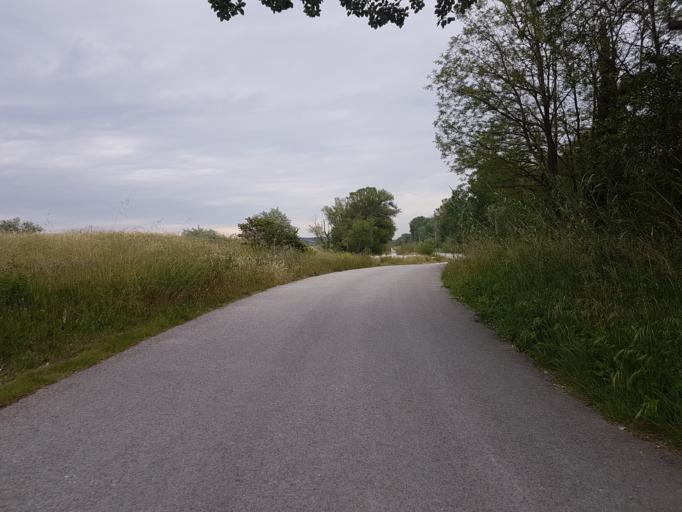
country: FR
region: Languedoc-Roussillon
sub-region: Departement du Gard
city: Montfaucon
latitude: 44.0687
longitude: 4.7700
